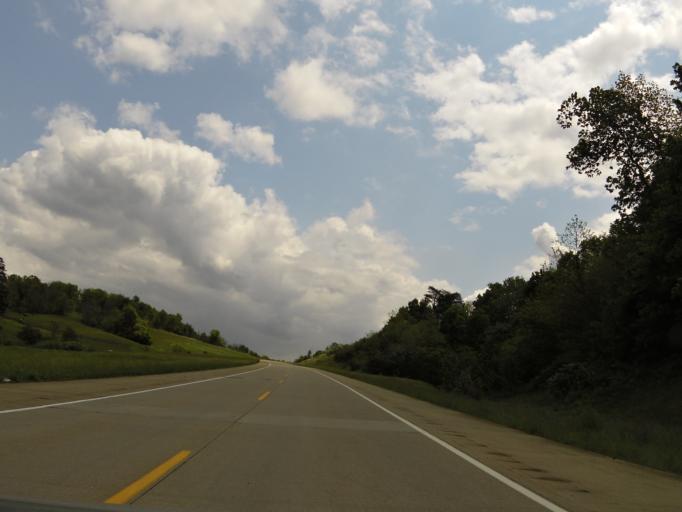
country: US
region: West Virginia
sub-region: Mason County
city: New Haven
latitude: 38.9993
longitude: -81.8829
